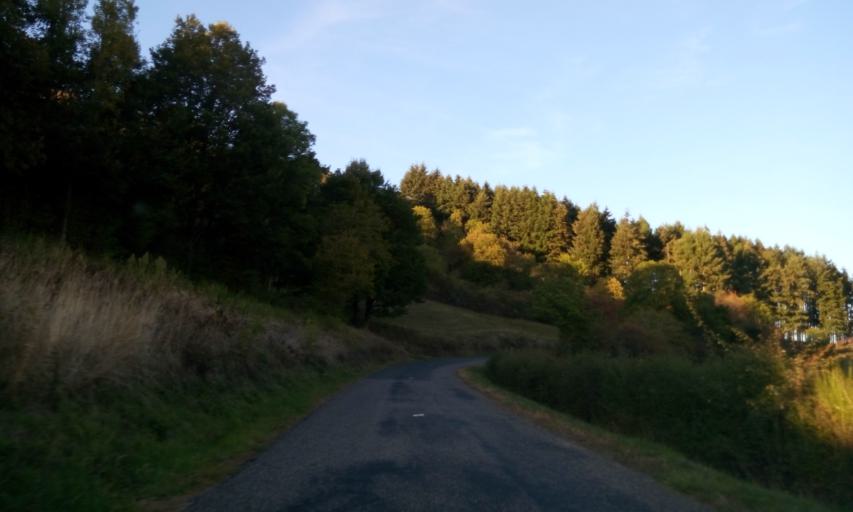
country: FR
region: Rhone-Alpes
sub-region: Departement du Rhone
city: Grandris
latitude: 45.9681
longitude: 4.4683
